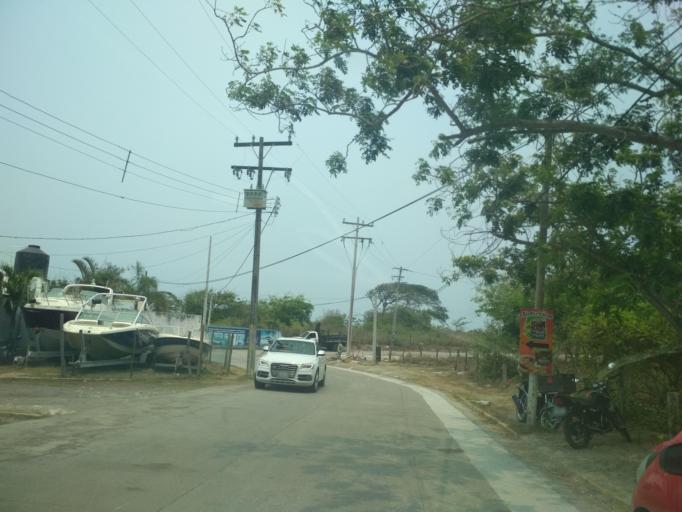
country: MX
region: Veracruz
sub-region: Alvarado
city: Playa de la Libertad
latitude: 19.0913
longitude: -96.0996
